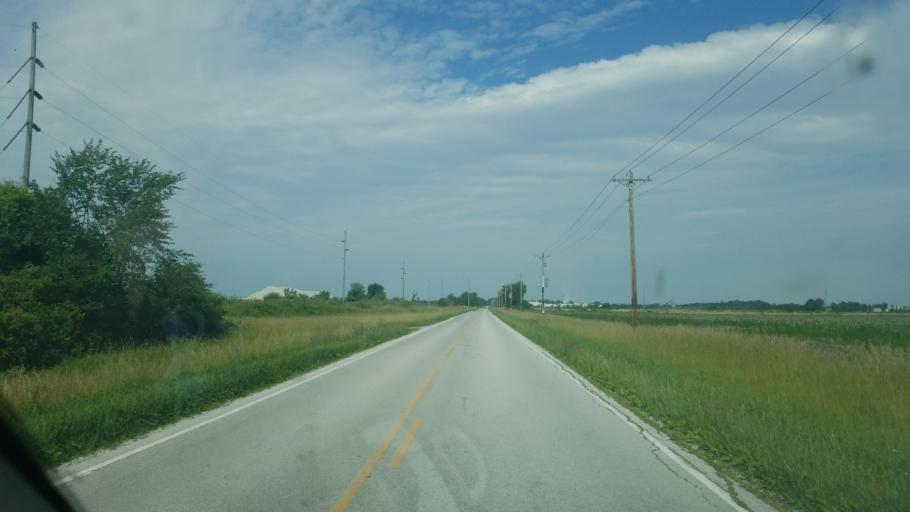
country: US
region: Ohio
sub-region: Wyandot County
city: Carey
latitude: 40.9635
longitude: -83.3431
